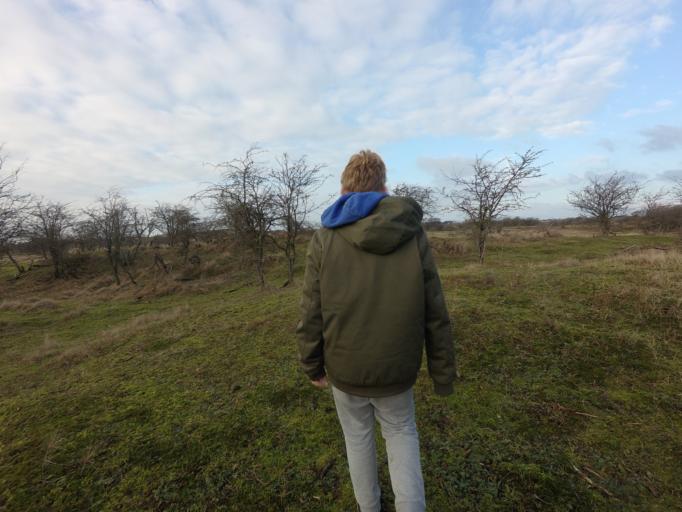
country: NL
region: North Holland
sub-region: Gemeente Zandvoort
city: Zandvoort
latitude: 52.3188
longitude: 4.5226
